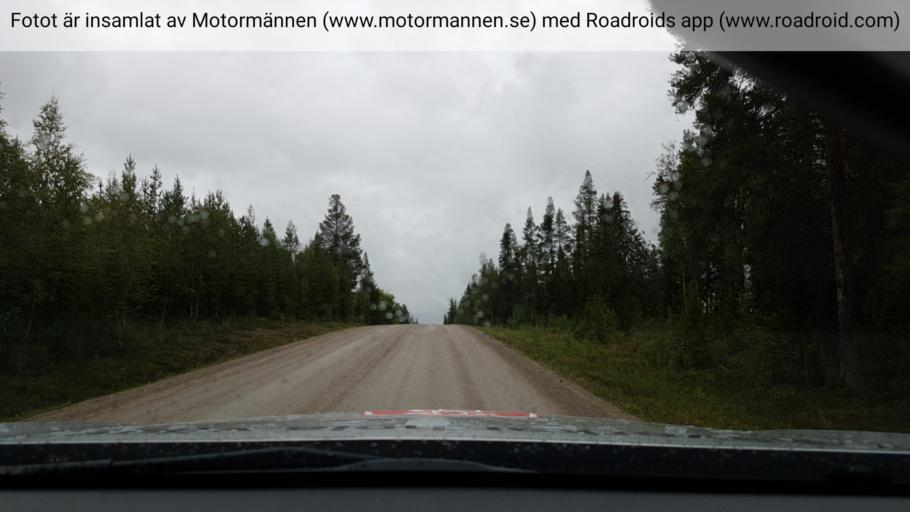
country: SE
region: Vaesterbotten
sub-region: Asele Kommun
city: Insjon
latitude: 64.7382
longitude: 17.6535
